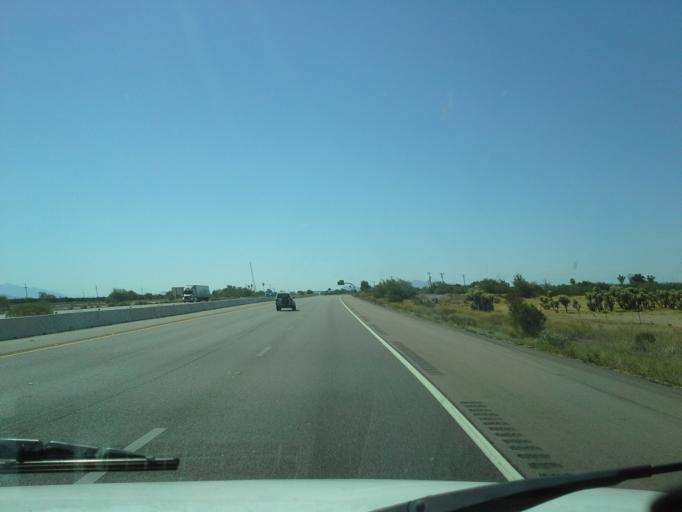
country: US
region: Arizona
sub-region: Pima County
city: Avra Valley
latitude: 32.5845
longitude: -111.3326
